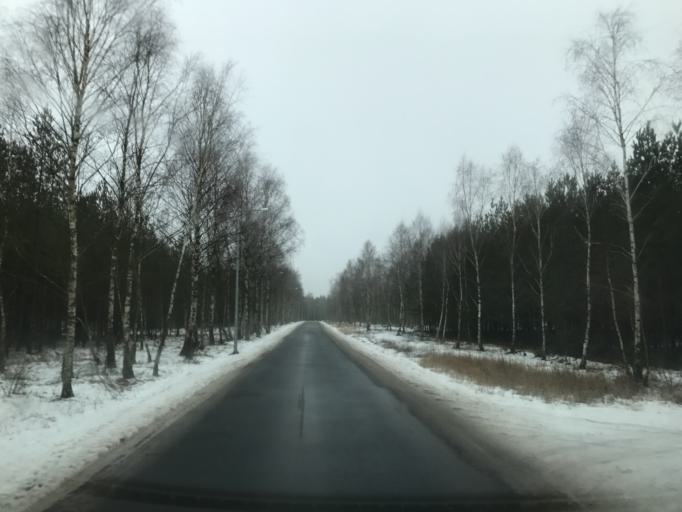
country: PL
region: Kujawsko-Pomorskie
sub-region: Powiat torunski
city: Wielka Nieszawka
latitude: 52.9878
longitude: 18.4516
